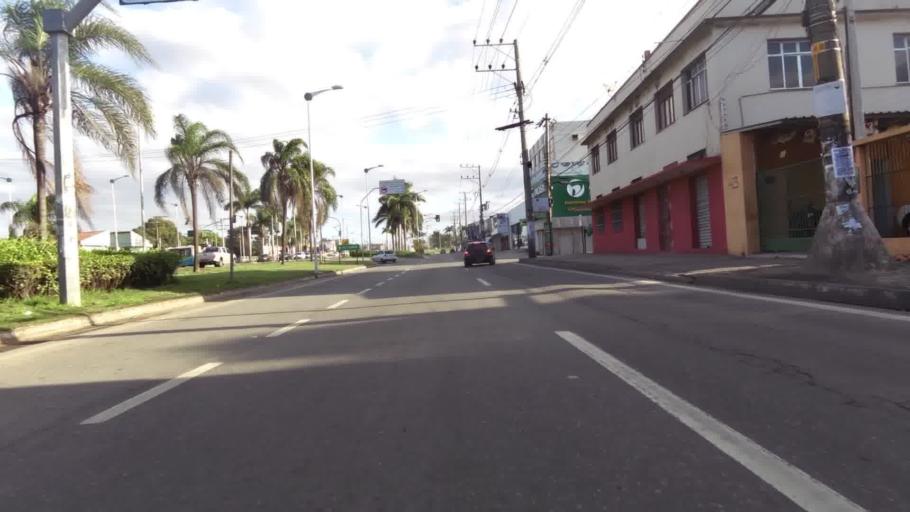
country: BR
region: Espirito Santo
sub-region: Vila Velha
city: Vila Velha
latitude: -20.2300
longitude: -40.2731
